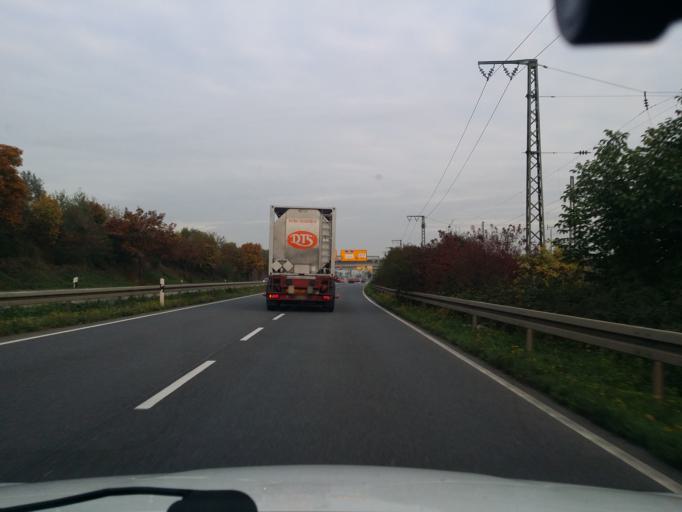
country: DE
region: Rheinland-Pfalz
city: Altrip
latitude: 49.4628
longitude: 8.5083
